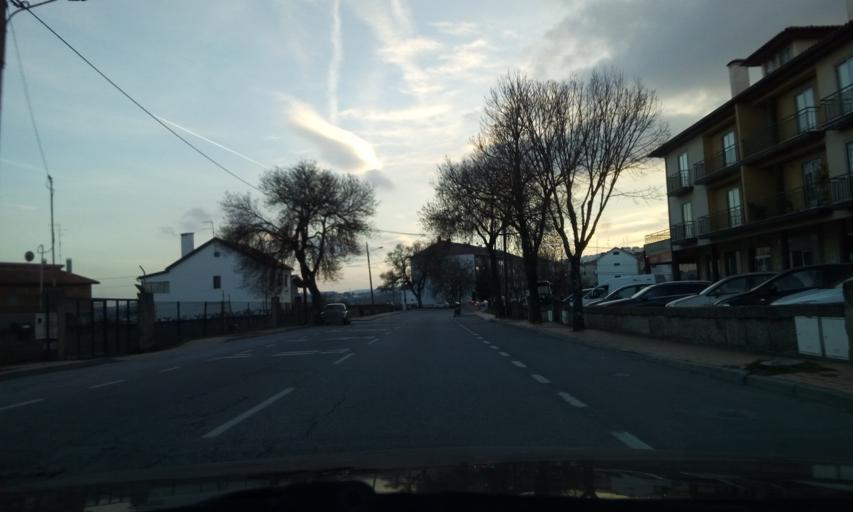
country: PT
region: Guarda
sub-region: Guarda
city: Sequeira
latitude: 40.5585
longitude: -7.2354
